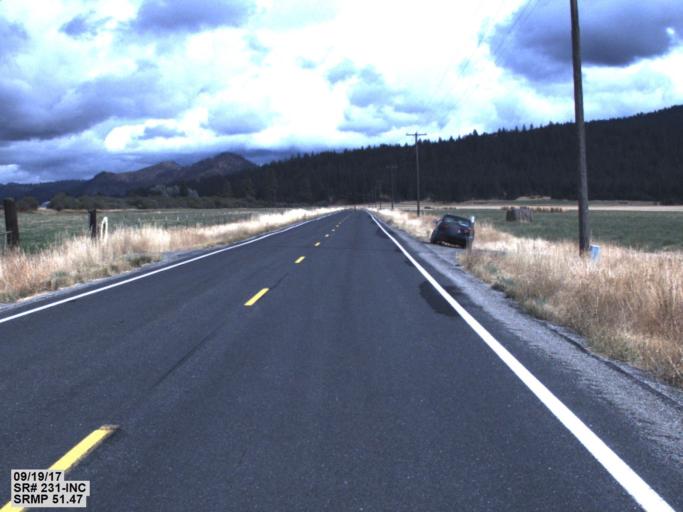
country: US
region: Washington
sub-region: Spokane County
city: Deer Park
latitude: 47.9190
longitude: -117.7906
